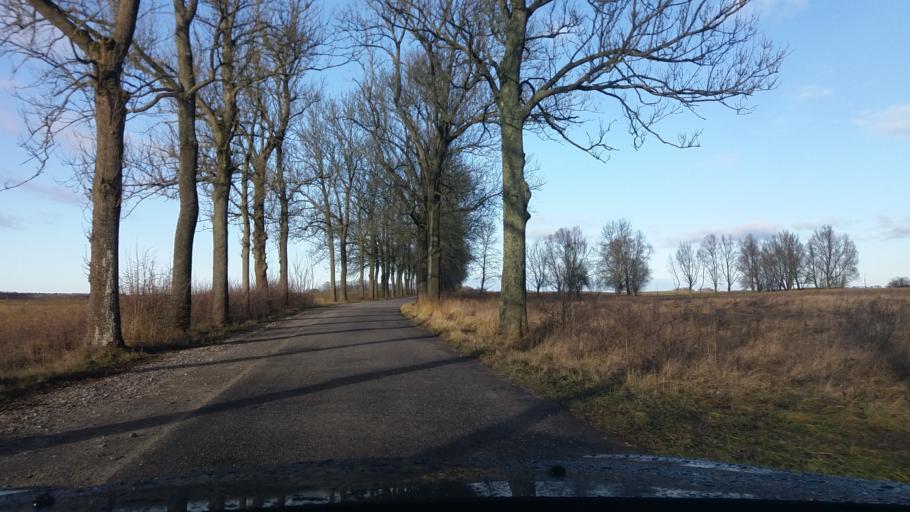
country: PL
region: West Pomeranian Voivodeship
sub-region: Powiat choszczenski
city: Drawno
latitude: 53.1842
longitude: 15.7990
